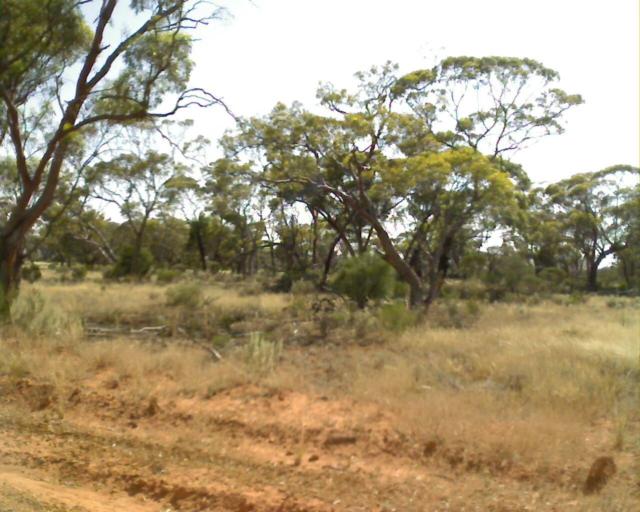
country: AU
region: Western Australia
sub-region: Merredin
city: Merredin
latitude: -30.9635
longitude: 118.8911
